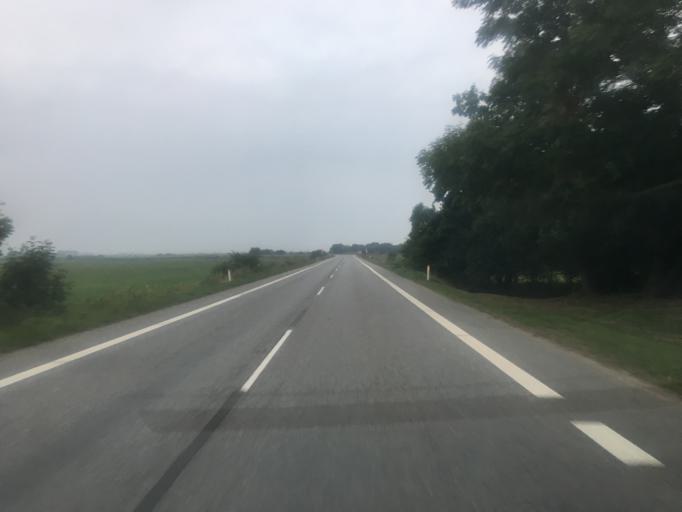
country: DK
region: South Denmark
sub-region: Tonder Kommune
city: Tonder
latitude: 54.9225
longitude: 8.8391
